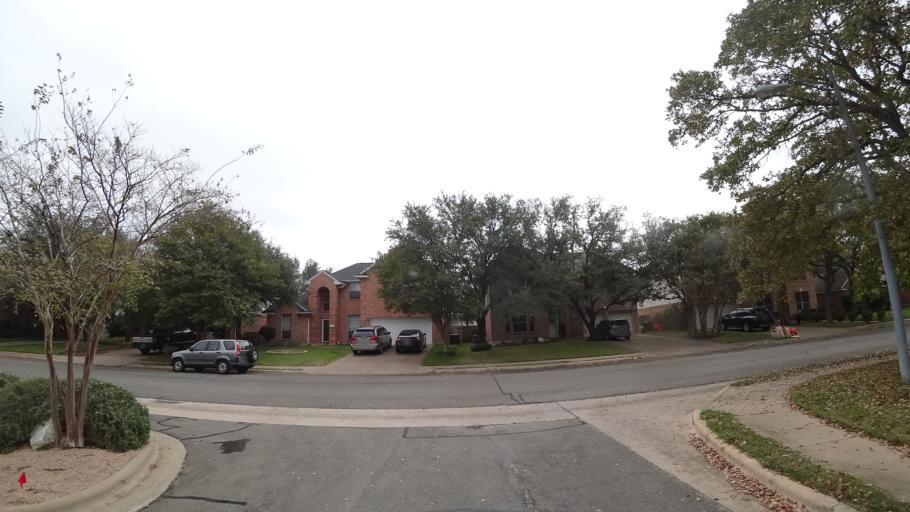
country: US
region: Texas
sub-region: Williamson County
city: Round Rock
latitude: 30.5135
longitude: -97.7048
